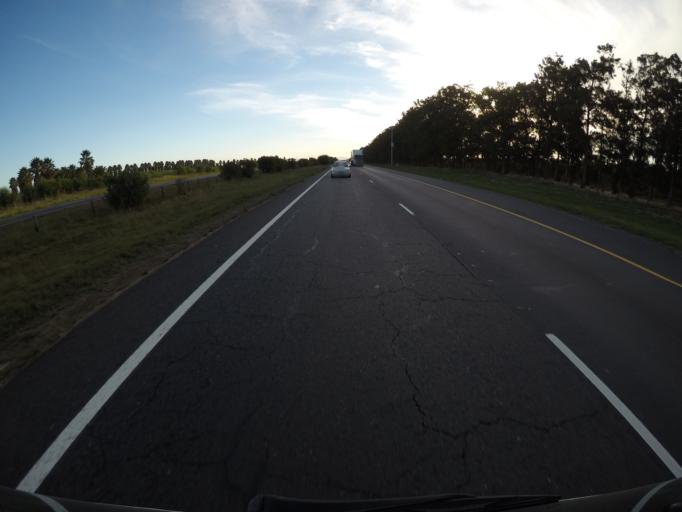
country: ZA
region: Western Cape
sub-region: City of Cape Town
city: Kraaifontein
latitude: -33.8238
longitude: 18.7773
